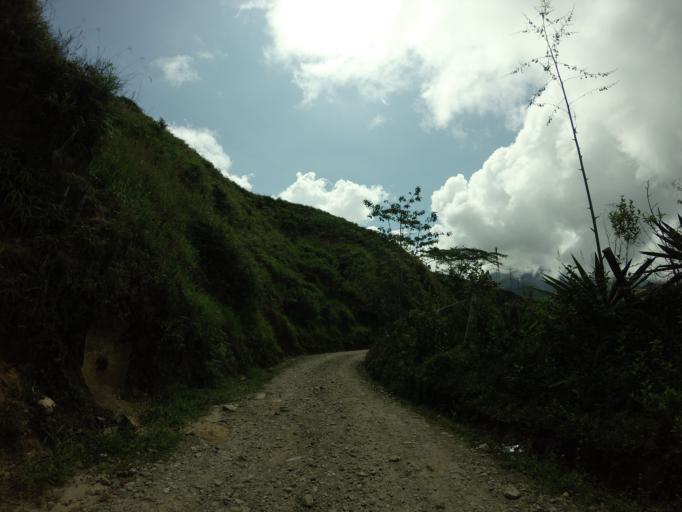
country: CO
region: Antioquia
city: Narino
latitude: 5.5032
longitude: -75.1816
